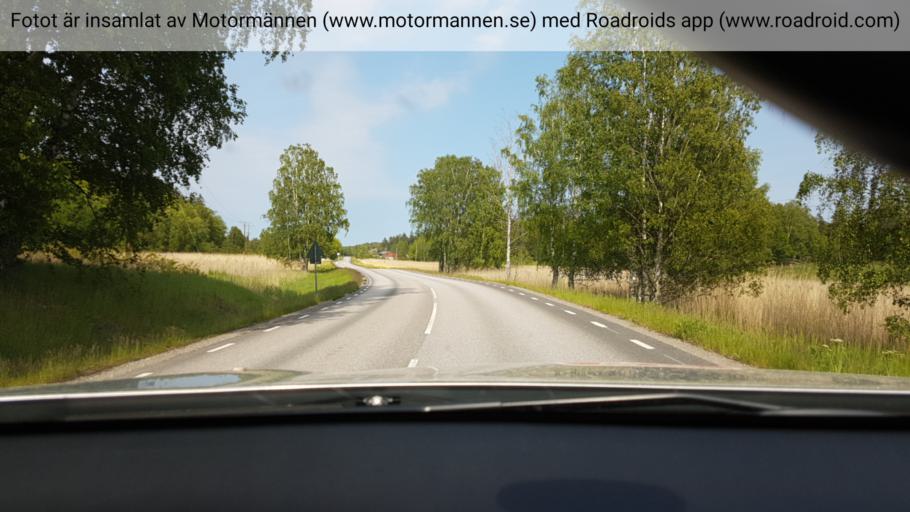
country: SE
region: Stockholm
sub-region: Nynashamns Kommun
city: Nynashamn
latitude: 58.9573
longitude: 17.9685
